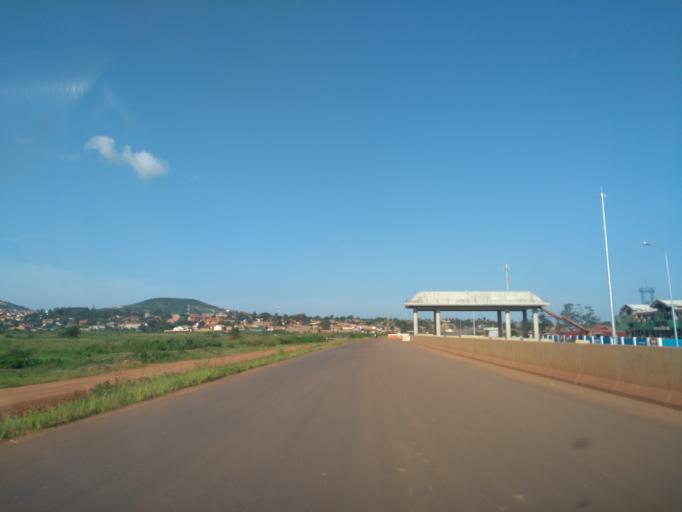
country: UG
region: Central Region
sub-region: Wakiso District
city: Kajansi
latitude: 0.2151
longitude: 32.5357
